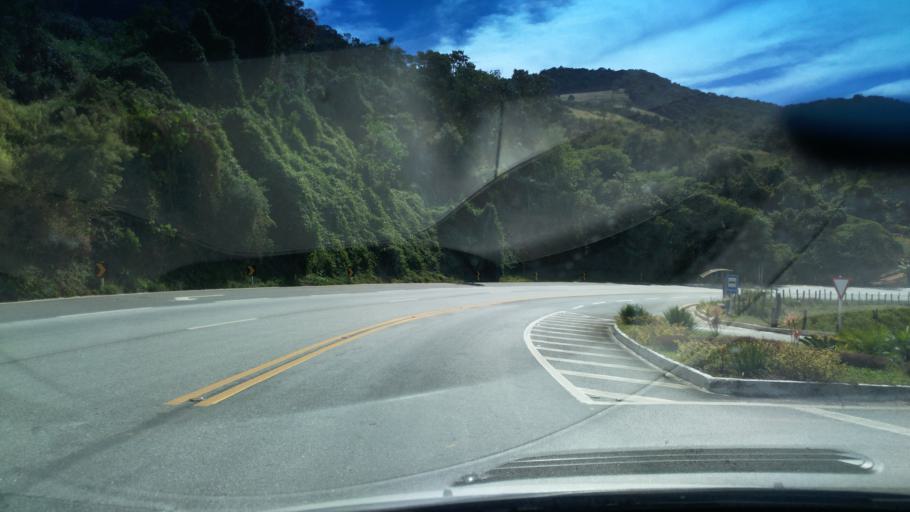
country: BR
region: Minas Gerais
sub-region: Borda Da Mata
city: Borda da Mata
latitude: -22.1334
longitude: -46.1565
